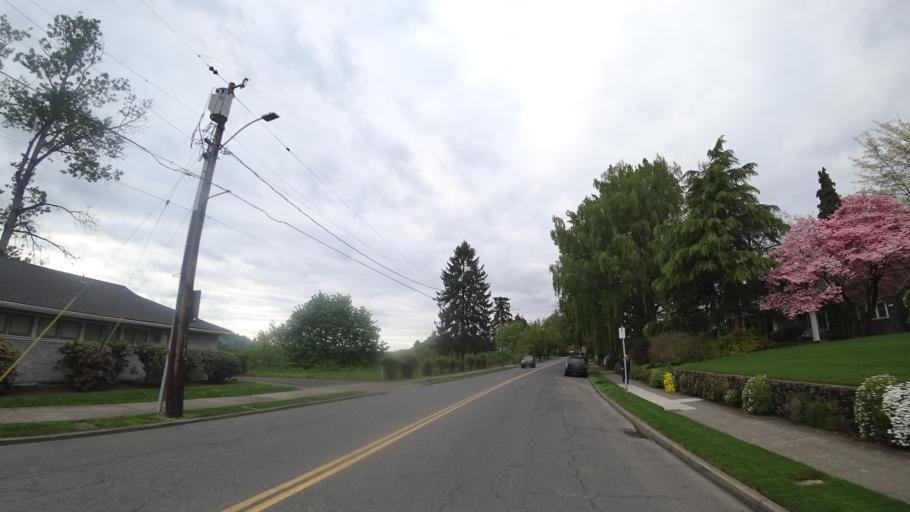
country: US
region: Oregon
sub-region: Clackamas County
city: Milwaukie
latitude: 45.4718
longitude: -122.6529
